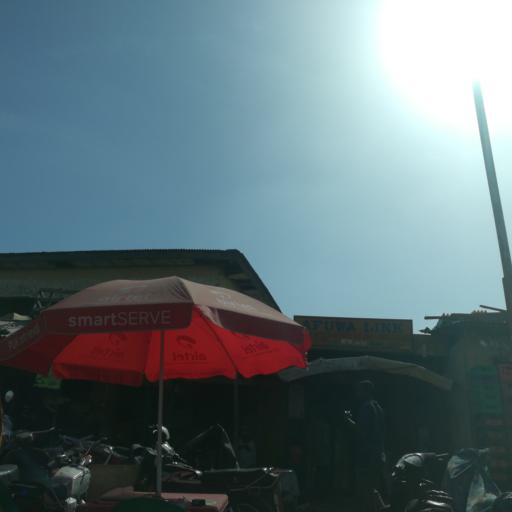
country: NG
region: Kano
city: Kano
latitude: 12.0051
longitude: 8.5236
